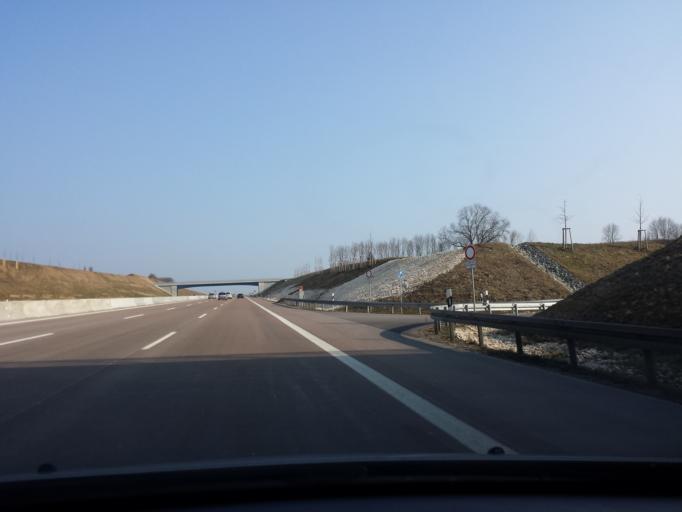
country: DE
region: Bavaria
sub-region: Swabia
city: Burgau
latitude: 48.4271
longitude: 10.3804
